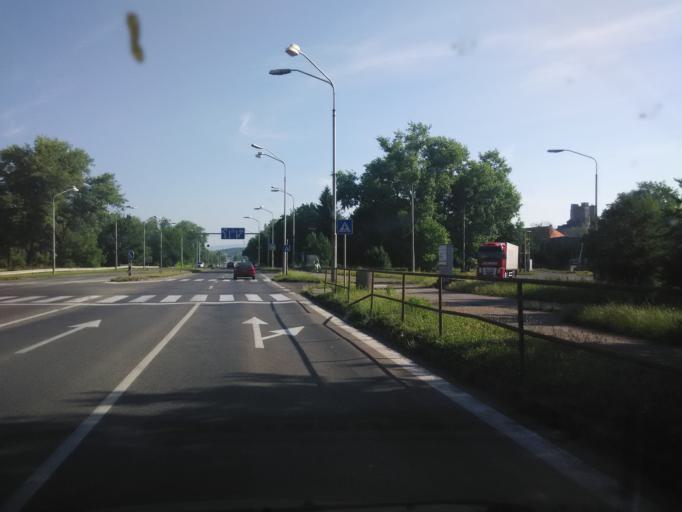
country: SK
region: Nitriansky
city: Levice
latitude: 48.2195
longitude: 18.5990
